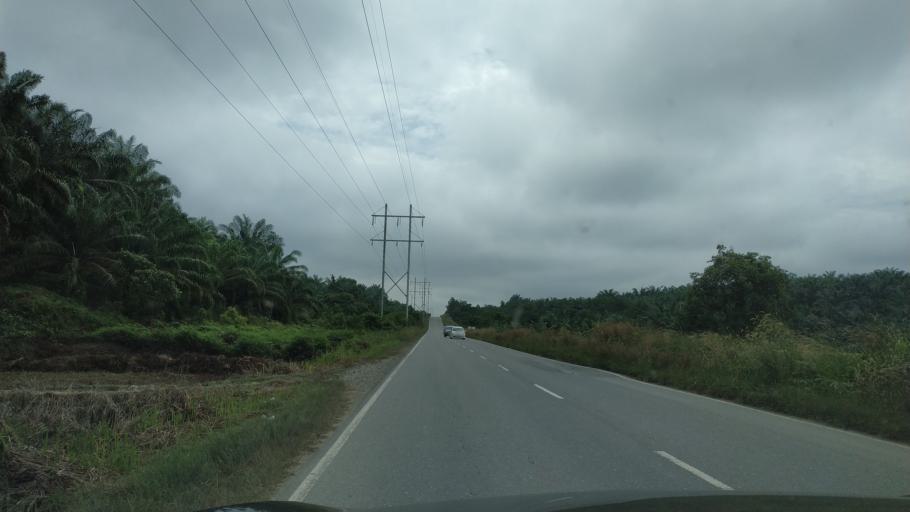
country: ID
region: Riau
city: Pekanbaru
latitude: 0.6435
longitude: 101.6718
